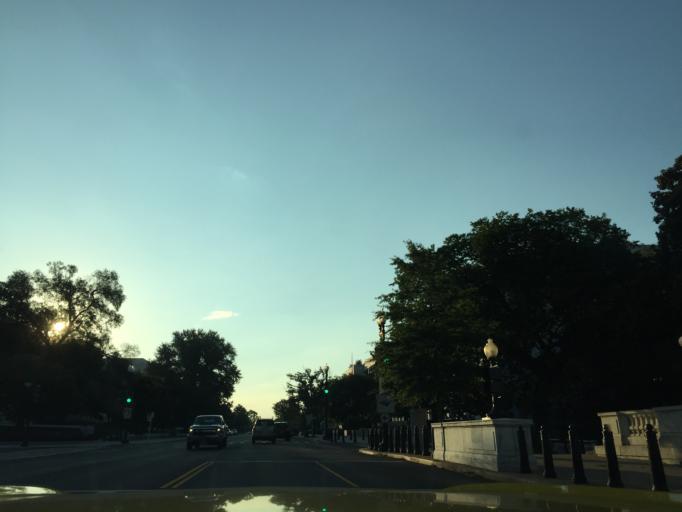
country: US
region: Washington, D.C.
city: Washington, D.C.
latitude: 38.8876
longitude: -77.0065
